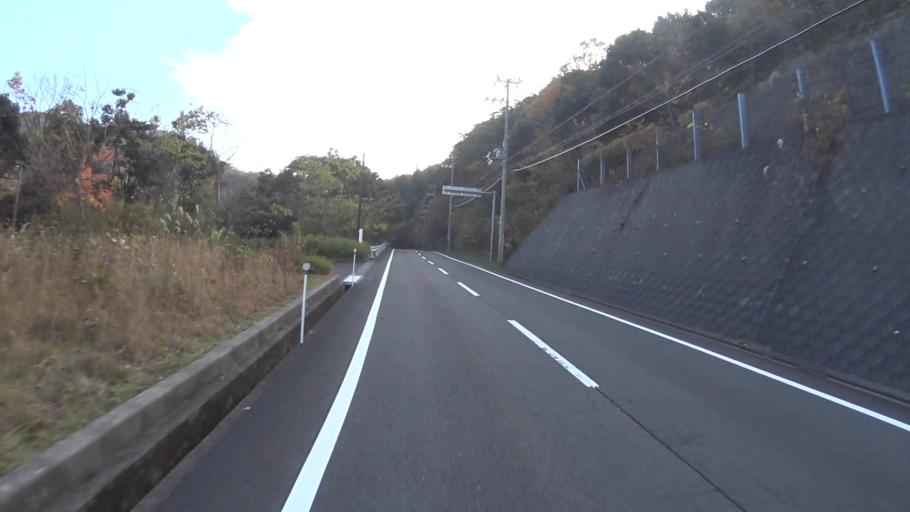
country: JP
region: Kyoto
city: Maizuru
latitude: 35.5445
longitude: 135.3959
